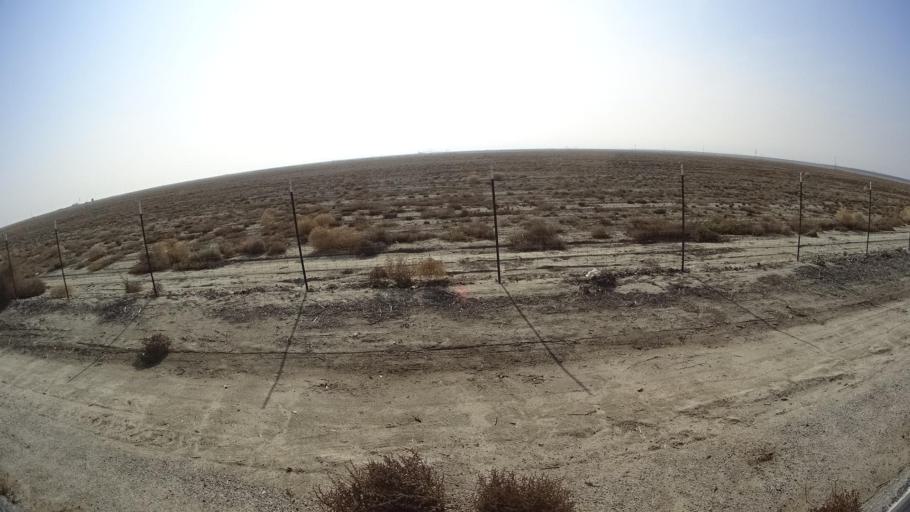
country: US
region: California
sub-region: Kern County
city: Buttonwillow
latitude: 35.3548
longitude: -119.3644
